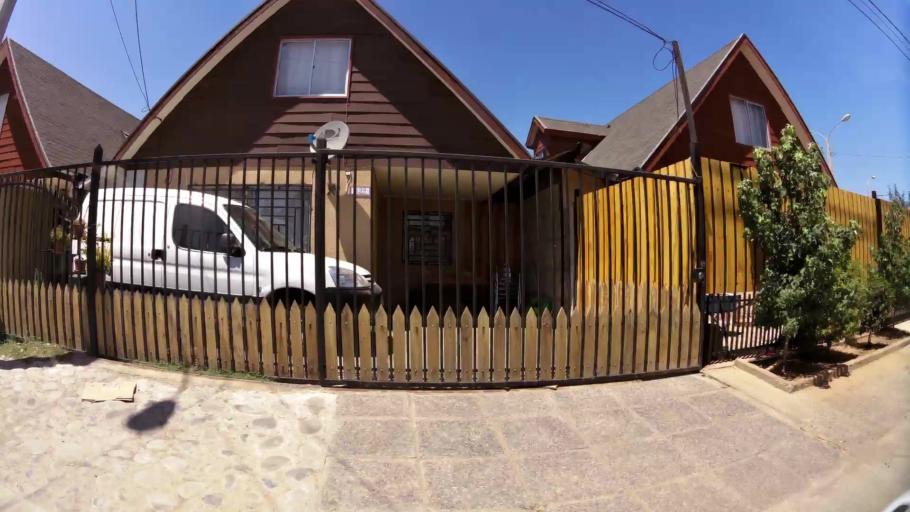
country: CL
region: Maule
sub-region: Provincia de Talca
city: Talca
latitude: -35.4447
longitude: -71.6176
